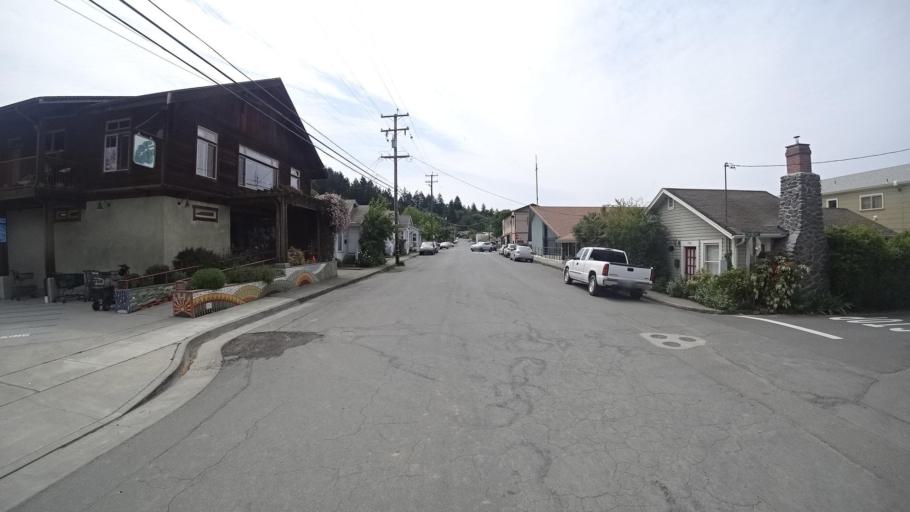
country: US
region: California
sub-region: Humboldt County
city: Redway
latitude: 40.1006
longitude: -123.7937
